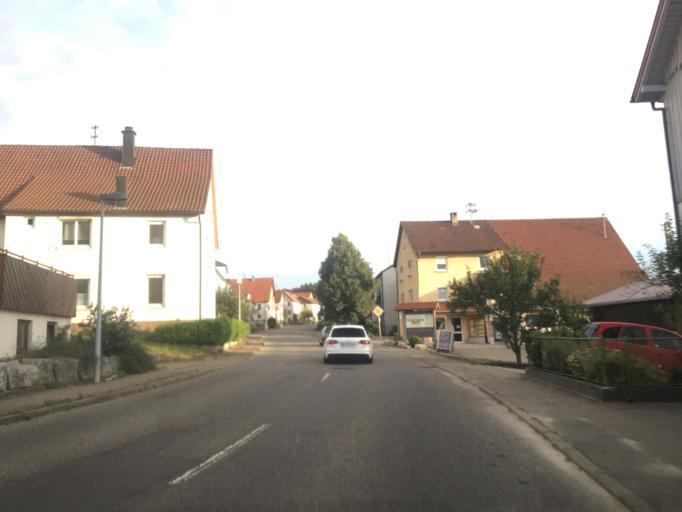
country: DE
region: Baden-Wuerttemberg
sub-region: Tuebingen Region
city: Sankt Johann
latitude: 48.4568
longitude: 9.3423
